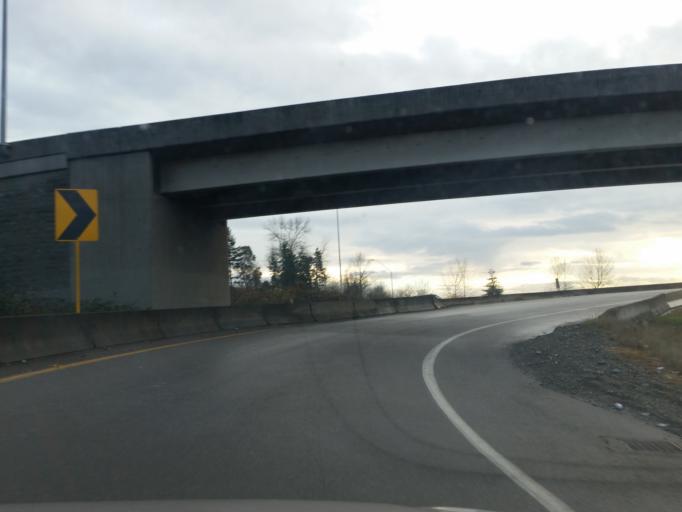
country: US
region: Washington
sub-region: King County
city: Renton
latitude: 47.4687
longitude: -122.2164
